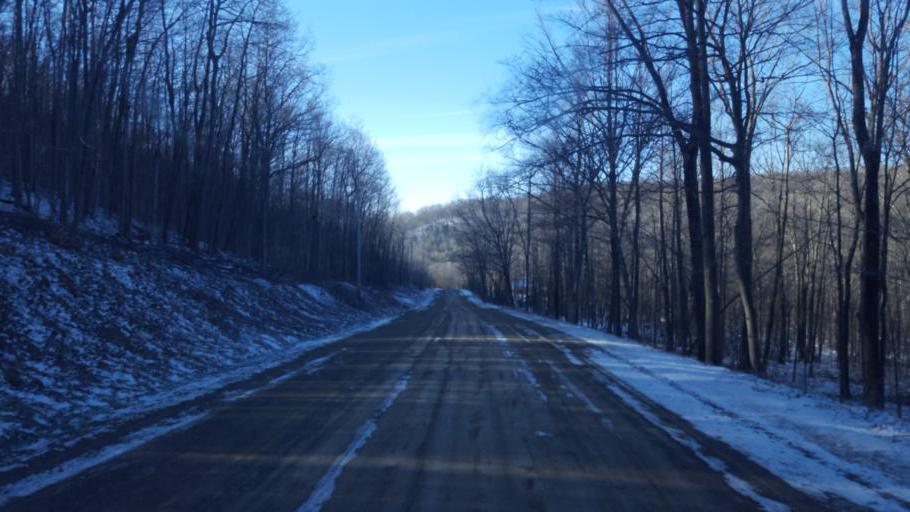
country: US
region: New York
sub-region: Allegany County
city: Wellsville
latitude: 42.1569
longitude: -77.9095
